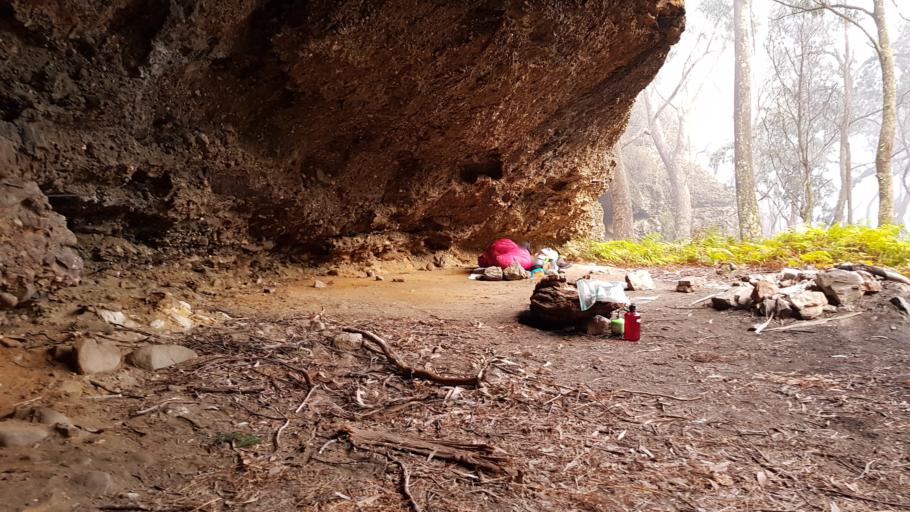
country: AU
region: New South Wales
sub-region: Shoalhaven Shire
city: Milton
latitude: -35.2785
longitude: 150.1274
